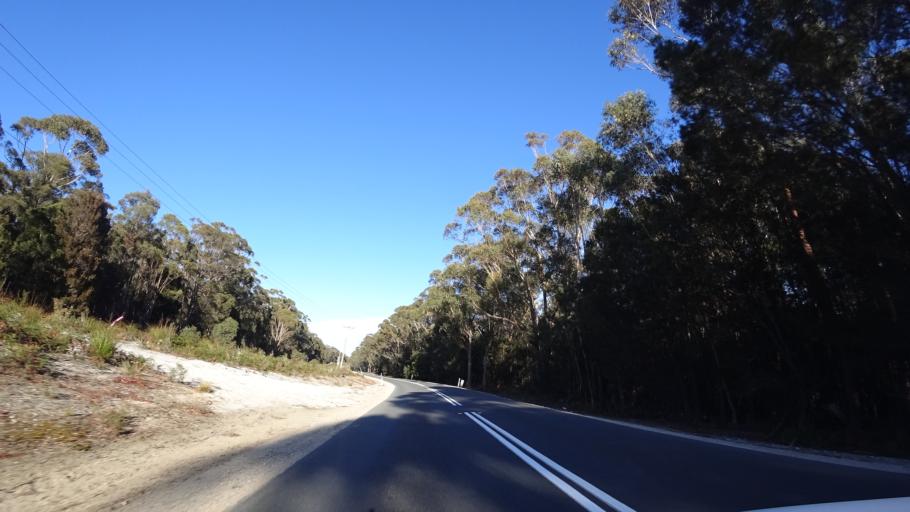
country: AU
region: Tasmania
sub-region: Break O'Day
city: St Helens
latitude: -41.2826
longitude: 148.1547
